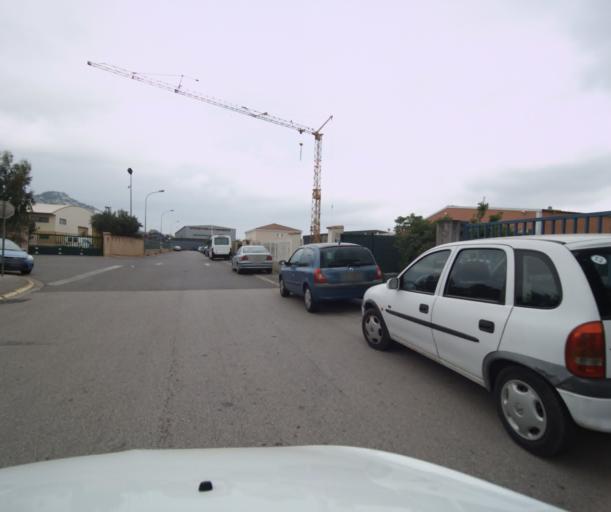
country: FR
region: Provence-Alpes-Cote d'Azur
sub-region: Departement du Var
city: La Crau
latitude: 43.1335
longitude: 6.0714
